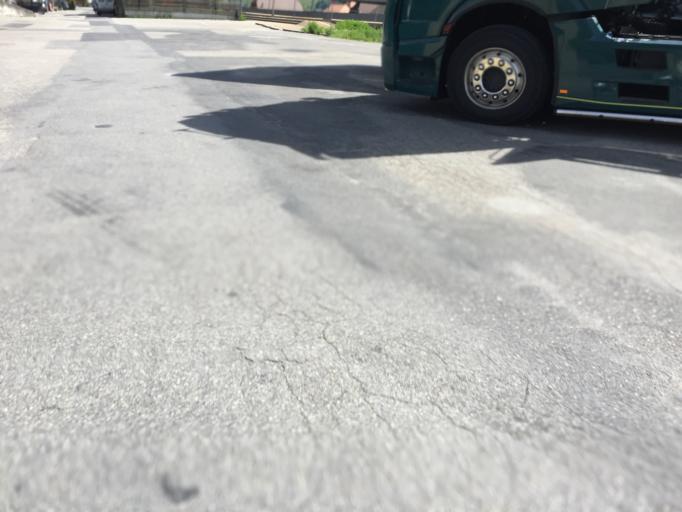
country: CH
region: Bern
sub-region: Emmental District
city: Signau
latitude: 46.9191
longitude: 7.7245
